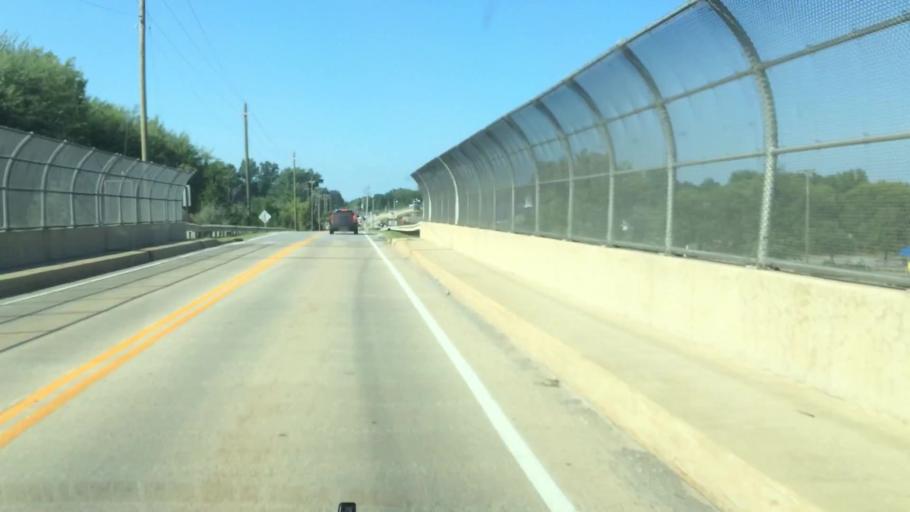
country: US
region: Ohio
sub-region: Cuyahoga County
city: Olmsted Falls
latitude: 41.3693
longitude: -81.9443
